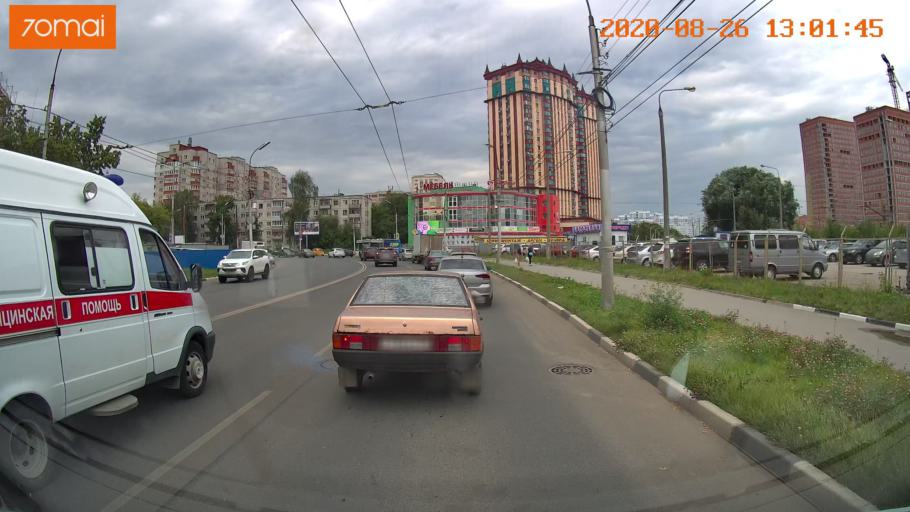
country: RU
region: Rjazan
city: Ryazan'
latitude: 54.6180
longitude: 39.7362
